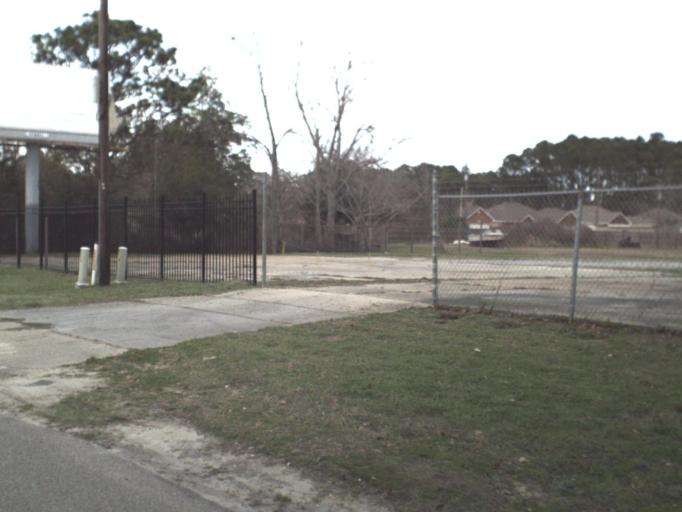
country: US
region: Florida
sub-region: Bay County
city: Hiland Park
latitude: 30.1942
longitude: -85.6249
